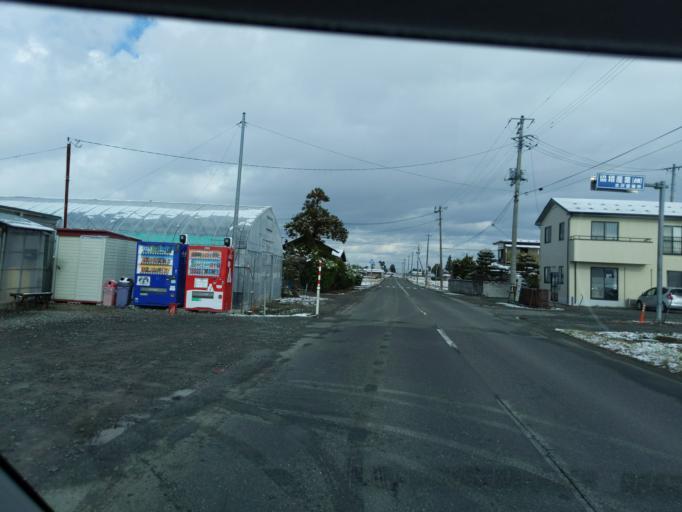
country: JP
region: Iwate
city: Mizusawa
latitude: 39.1507
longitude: 141.1134
